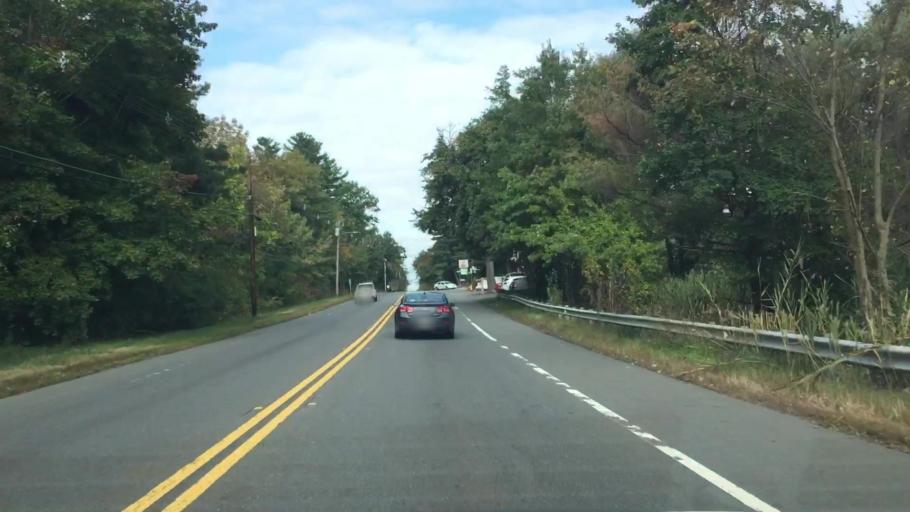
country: US
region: Massachusetts
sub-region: Essex County
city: Middleton
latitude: 42.6200
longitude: -71.0515
